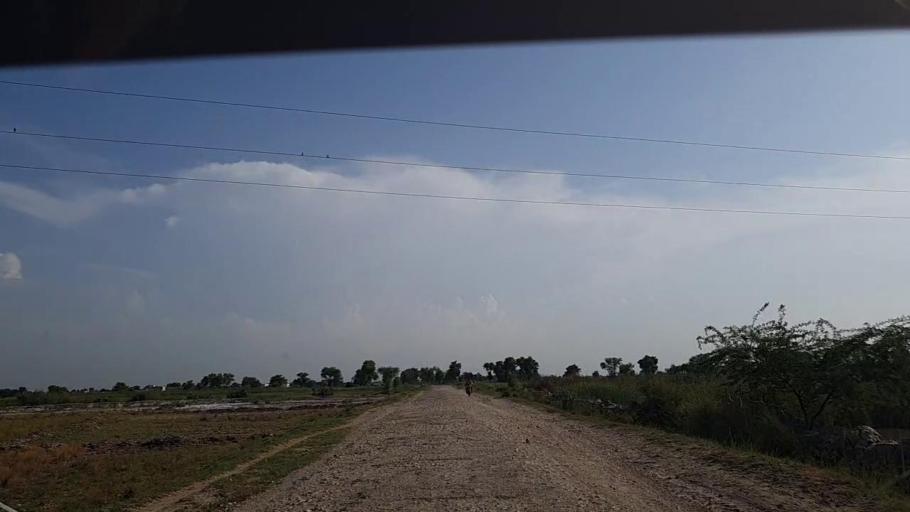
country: PK
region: Sindh
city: Khanpur
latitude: 27.8447
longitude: 69.3762
